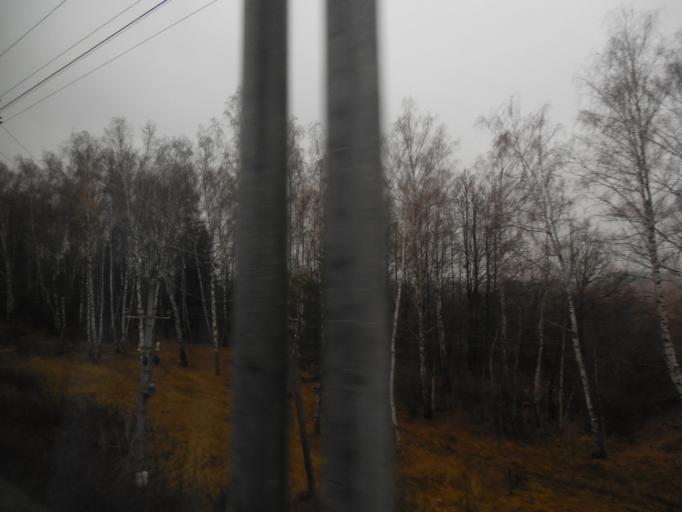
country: RU
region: Moskovskaya
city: Belyye Stolby
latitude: 55.3461
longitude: 37.8412
